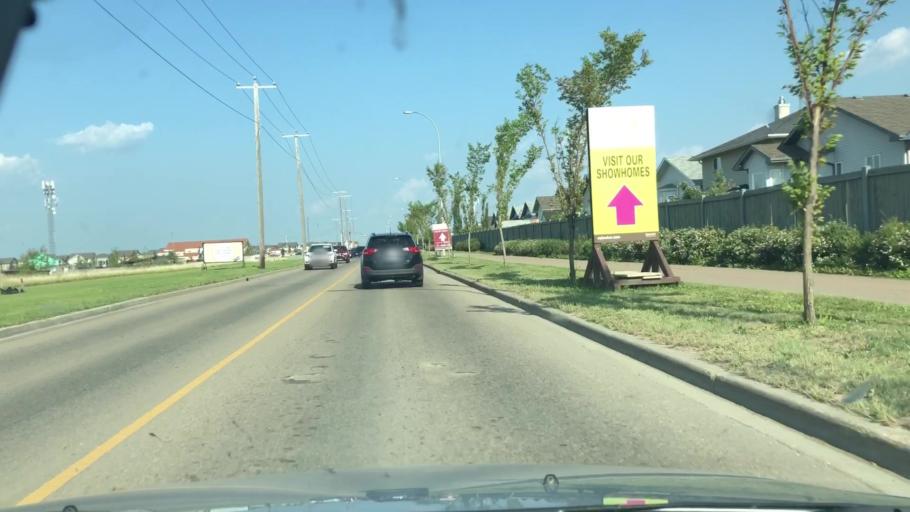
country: CA
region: Alberta
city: Edmonton
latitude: 53.6287
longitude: -113.4481
